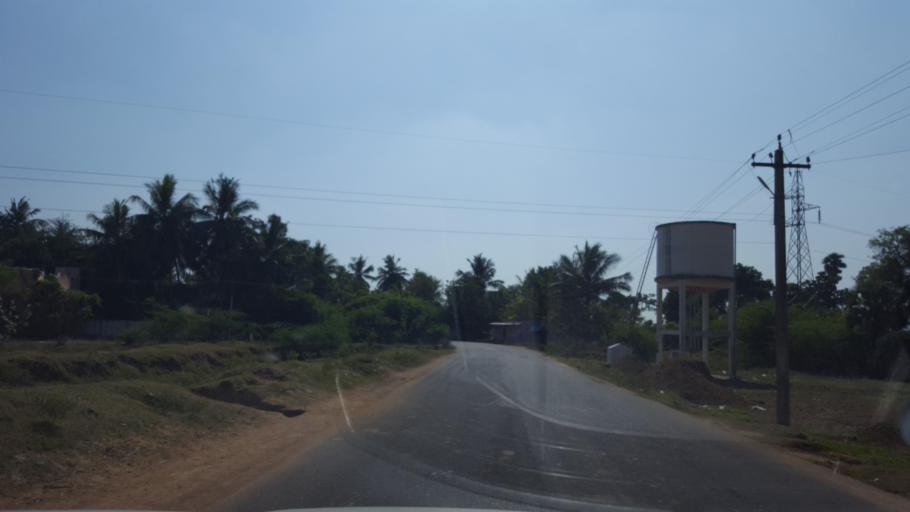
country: IN
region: Tamil Nadu
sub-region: Kancheepuram
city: Kanchipuram
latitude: 12.8380
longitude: 79.7400
